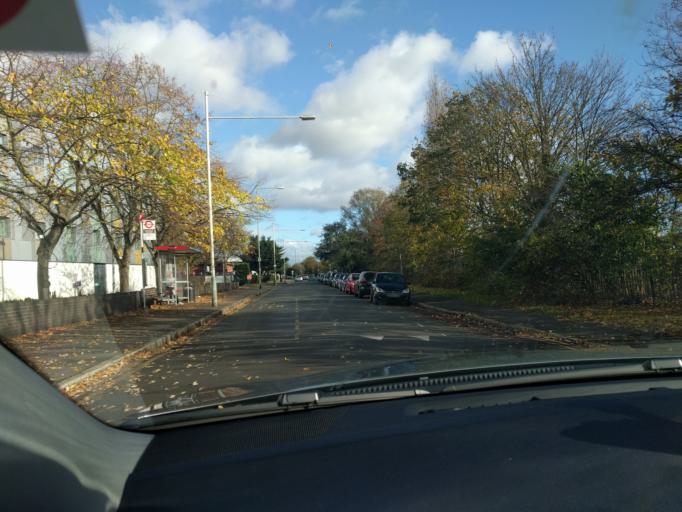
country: GB
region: England
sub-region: Greater London
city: West Drayton
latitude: 51.4815
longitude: -0.4821
